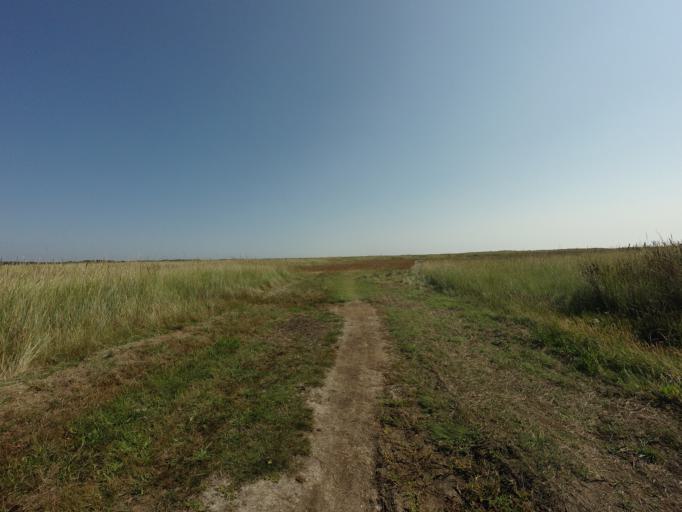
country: NL
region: Friesland
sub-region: Gemeente Schiermonnikoog
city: Schiermonnikoog
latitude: 53.4906
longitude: 6.2371
